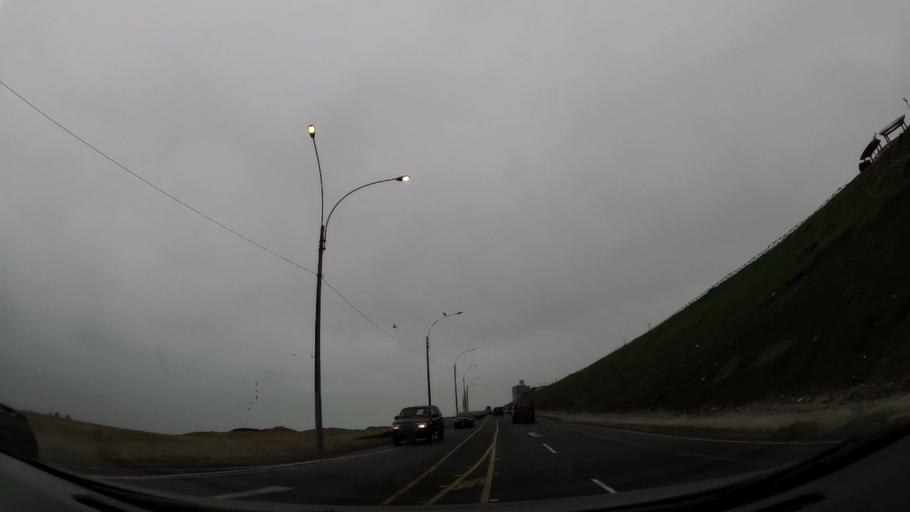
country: PE
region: Callao
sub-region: Callao
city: Callao
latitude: -12.0891
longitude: -77.0906
